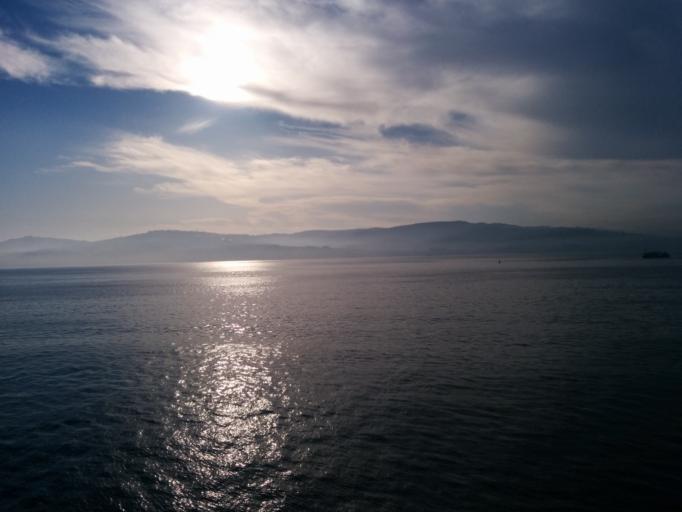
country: MA
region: Tanger-Tetouan
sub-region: Tanger-Assilah
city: Tangier
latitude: 35.7978
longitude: -5.7875
